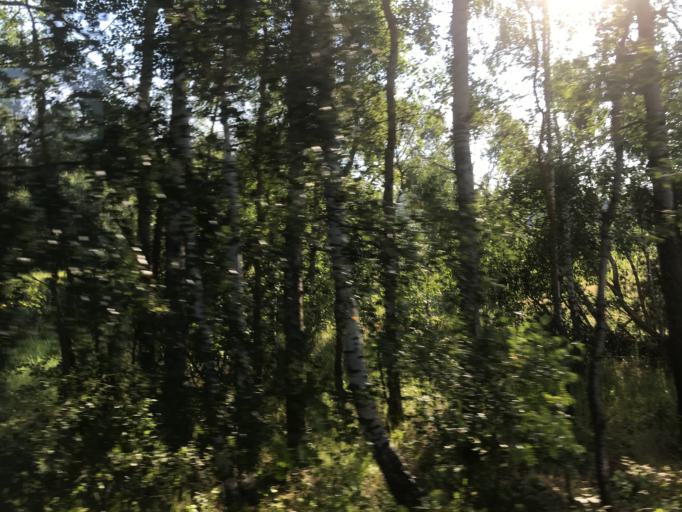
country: CZ
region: Jihocesky
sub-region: Okres Tabor
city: Veseli nad Luznici
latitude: 49.1556
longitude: 14.7241
